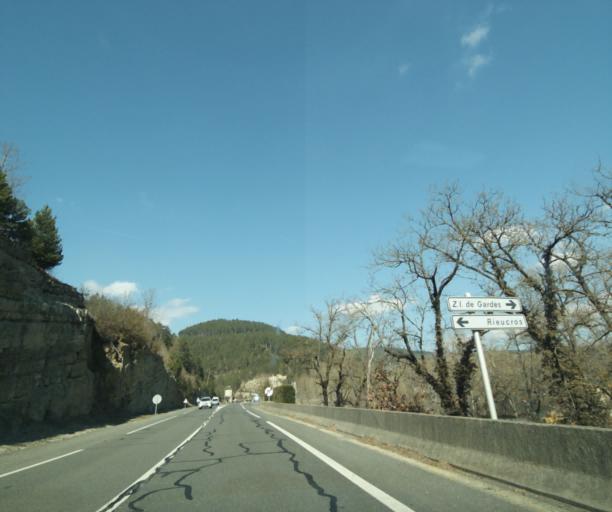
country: FR
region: Languedoc-Roussillon
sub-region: Departement de la Lozere
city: Mende
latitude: 44.5249
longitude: 3.5215
